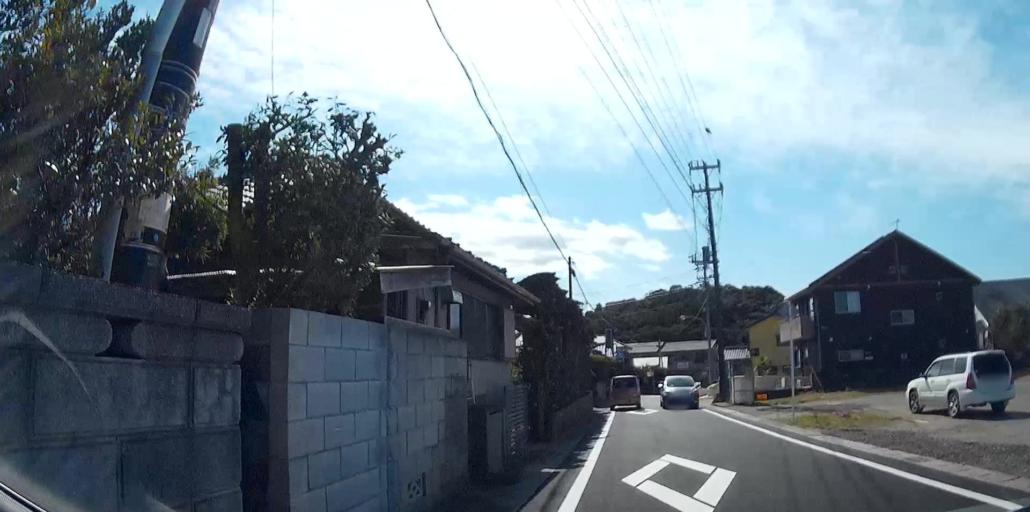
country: JP
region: Chiba
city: Tateyama
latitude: 35.0360
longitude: 139.8510
